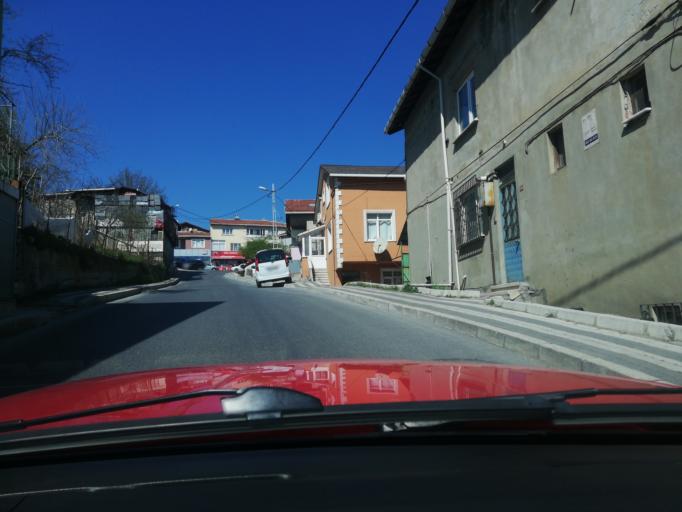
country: TR
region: Istanbul
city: Mahmut Sevket Pasa
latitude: 41.1158
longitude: 29.1150
